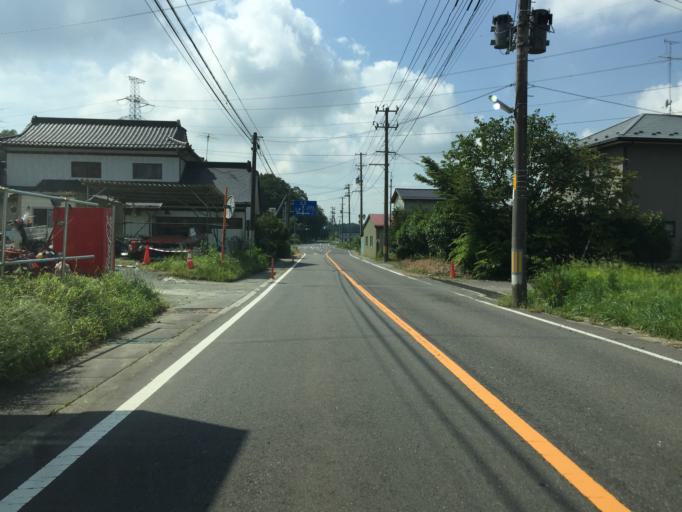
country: JP
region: Fukushima
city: Motomiya
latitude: 37.5407
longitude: 140.4038
